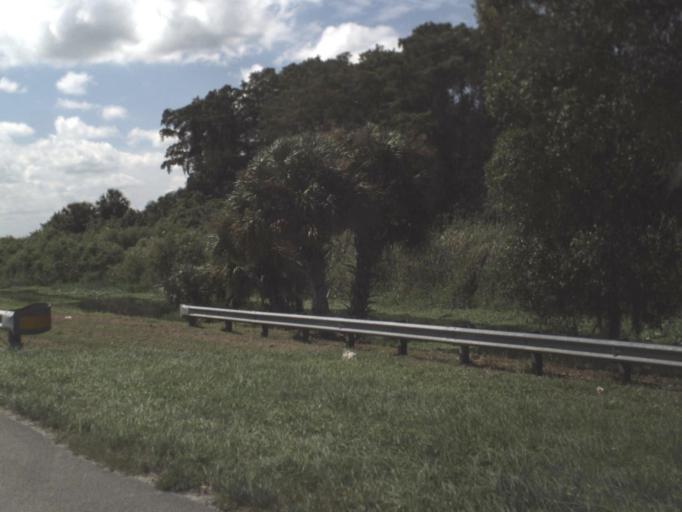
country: US
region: Florida
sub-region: Hendry County
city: LaBelle
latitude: 26.7214
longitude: -81.4376
